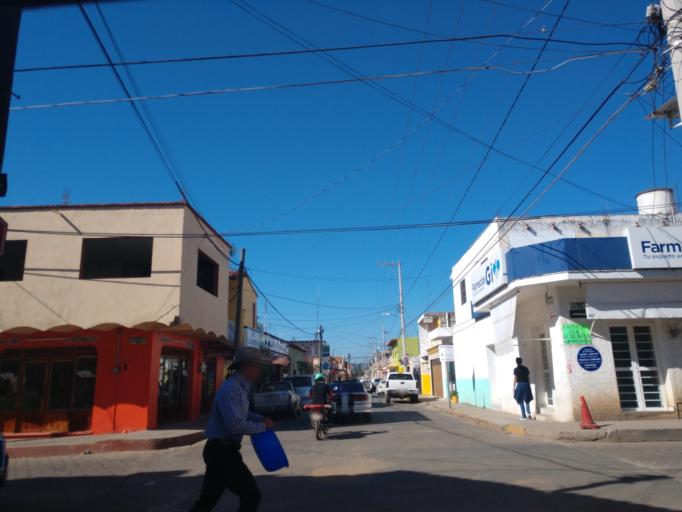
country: MX
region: Nayarit
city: Compostela
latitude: 21.2387
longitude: -104.9016
